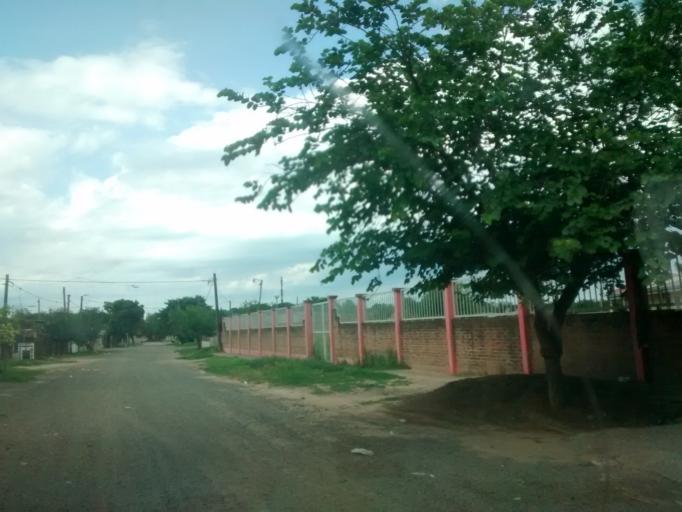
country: AR
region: Chaco
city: Resistencia
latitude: -27.4257
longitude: -58.9752
